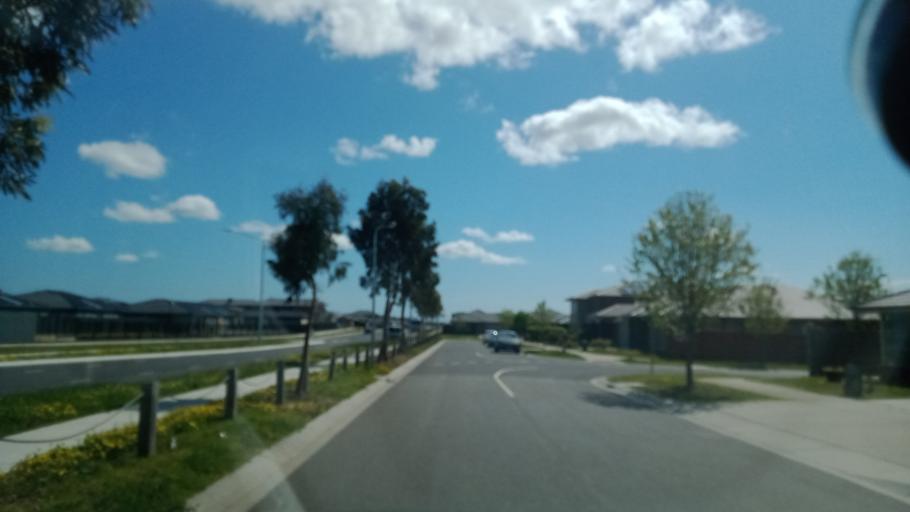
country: AU
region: Victoria
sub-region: Casey
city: Cranbourne West
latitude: -38.1018
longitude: 145.2530
